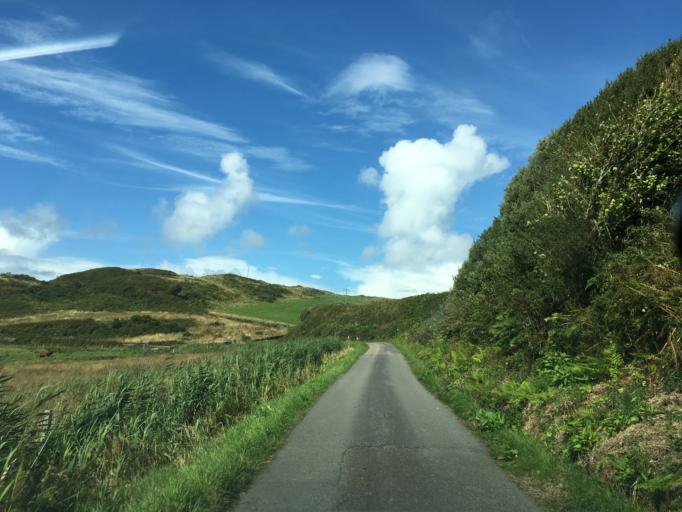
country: GB
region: Scotland
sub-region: Argyll and Bute
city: Isle Of Mull
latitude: 56.2481
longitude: -5.6443
